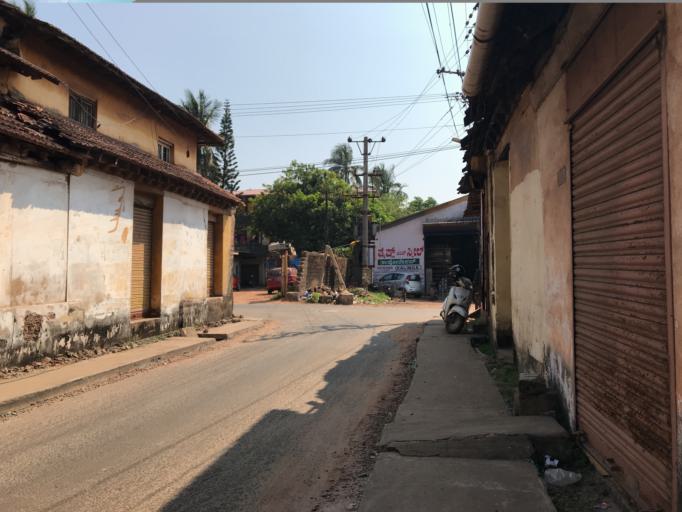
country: IN
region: Karnataka
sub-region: Dakshina Kannada
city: Mangalore
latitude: 12.8705
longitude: 74.8329
